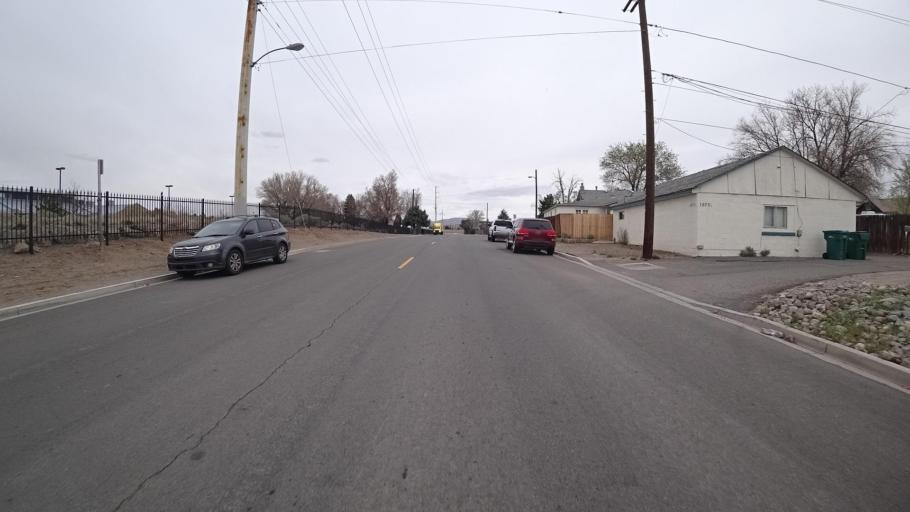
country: US
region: Nevada
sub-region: Washoe County
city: Sparks
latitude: 39.5306
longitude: -119.7714
